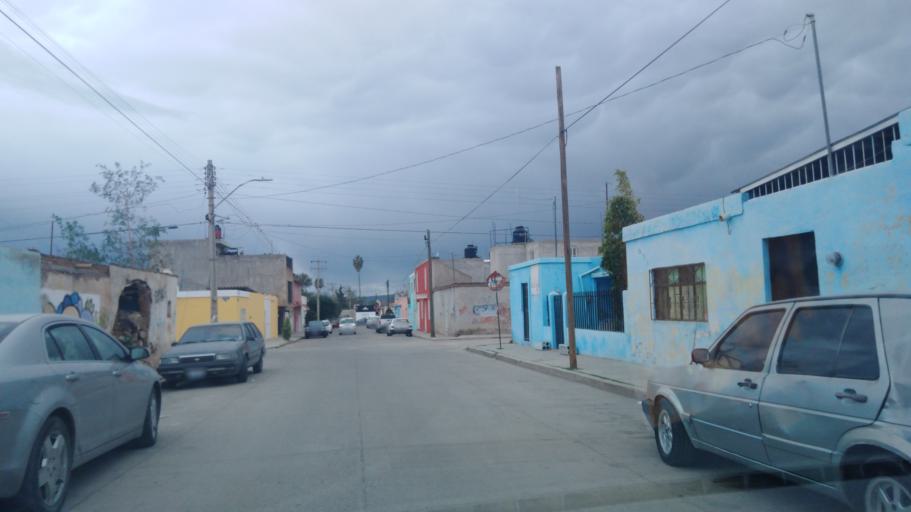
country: MX
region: Durango
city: Victoria de Durango
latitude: 24.0403
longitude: -104.6698
